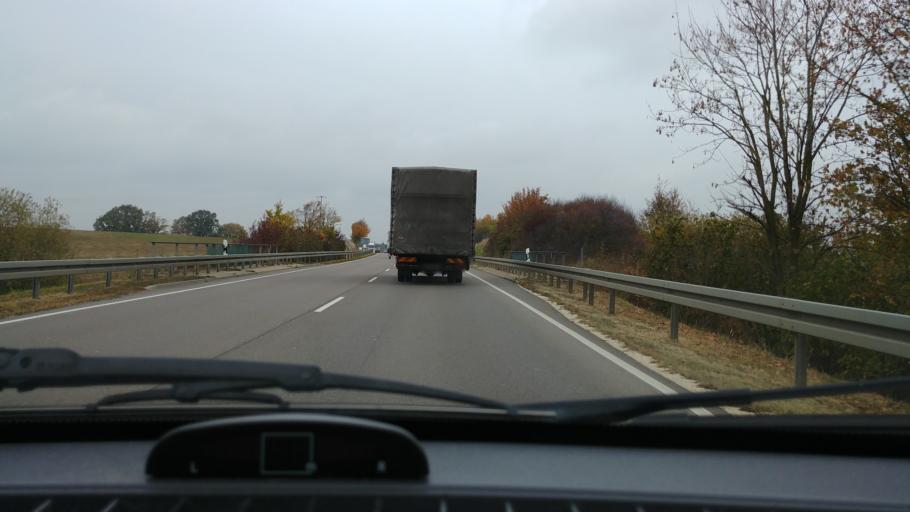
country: DE
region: Baden-Wuerttemberg
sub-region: Regierungsbezirk Stuttgart
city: Aalen
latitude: 48.8655
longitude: 10.0760
